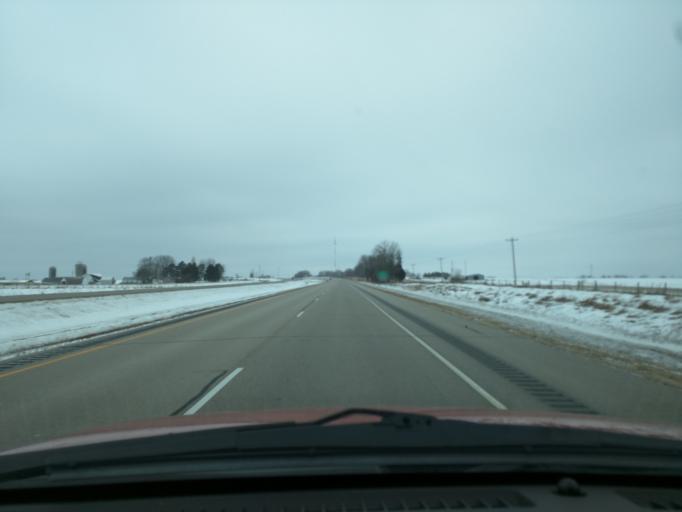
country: US
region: Wisconsin
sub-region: Trempealeau County
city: Trempealeau
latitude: 43.9117
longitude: -91.5436
